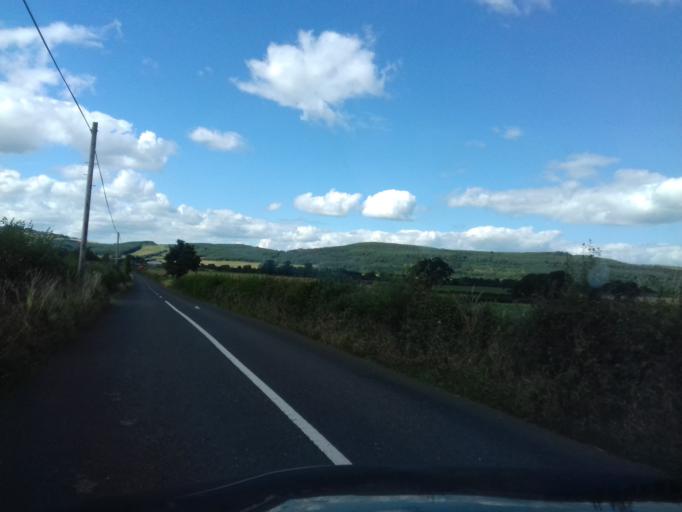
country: IE
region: Munster
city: Carrick-on-Suir
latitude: 52.3754
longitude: -7.4516
